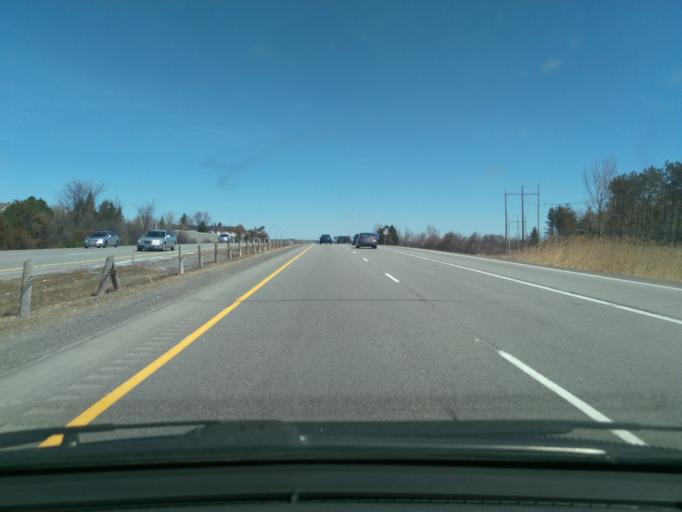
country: CA
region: Ontario
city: Ottawa
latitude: 45.4450
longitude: -75.5878
